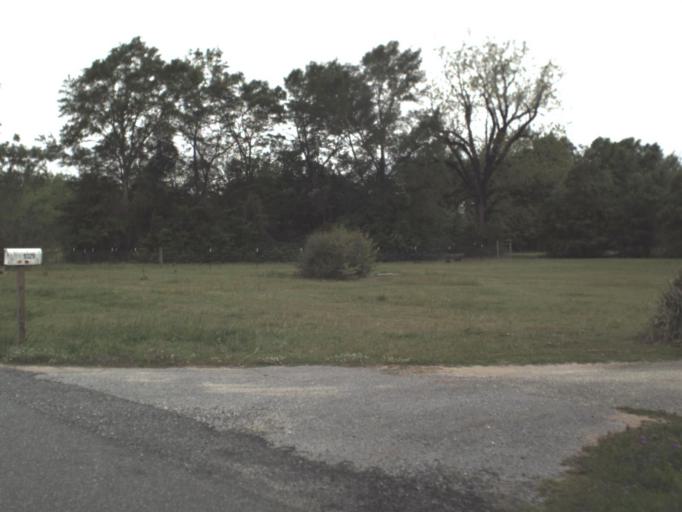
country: US
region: Florida
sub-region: Santa Rosa County
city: Point Baker
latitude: 30.7744
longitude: -87.0419
